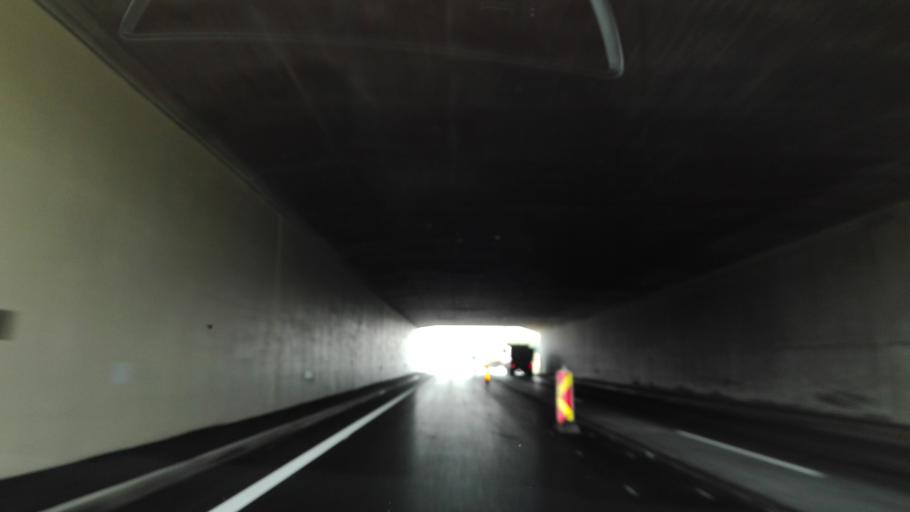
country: AT
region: Burgenland
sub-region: Politischer Bezirk Neusiedl am See
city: Zurndorf
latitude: 47.9403
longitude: 16.9640
